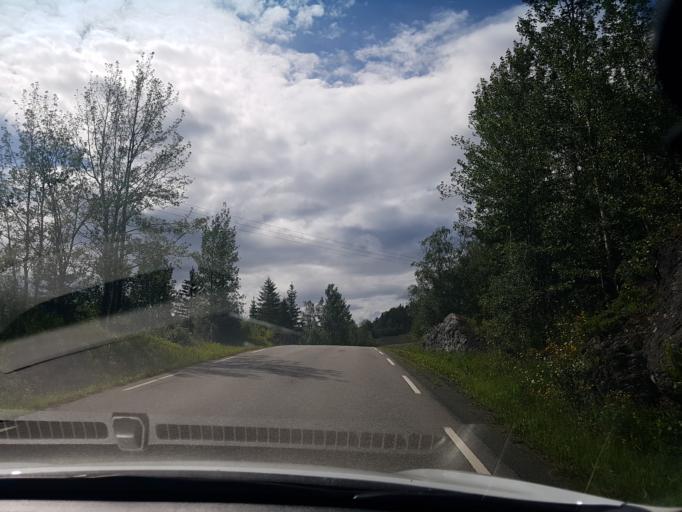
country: NO
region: Nord-Trondelag
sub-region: Stjordal
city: Stjordalshalsen
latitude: 63.5902
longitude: 10.9945
